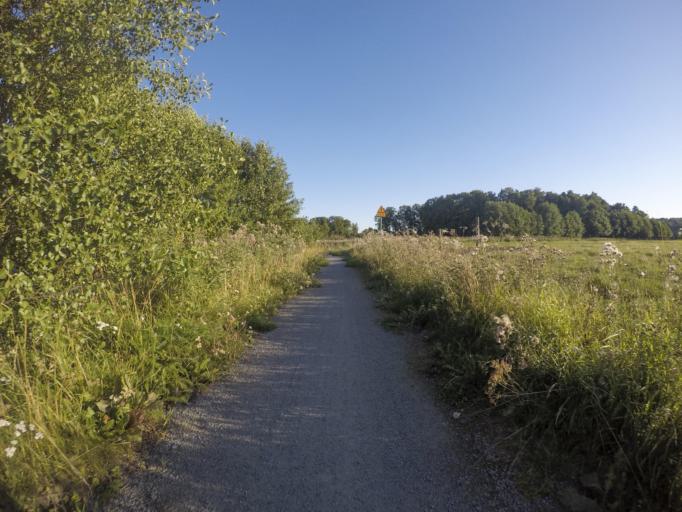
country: SE
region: Vaestmanland
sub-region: Vasteras
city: Vasteras
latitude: 59.5595
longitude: 16.6491
